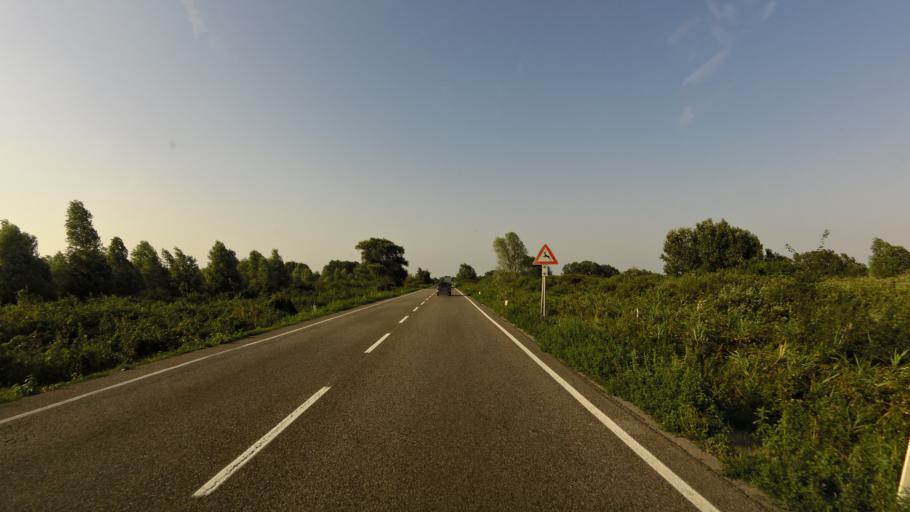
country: IT
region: Emilia-Romagna
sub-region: Provincia di Ravenna
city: Marina Romea
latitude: 44.5354
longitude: 12.2323
